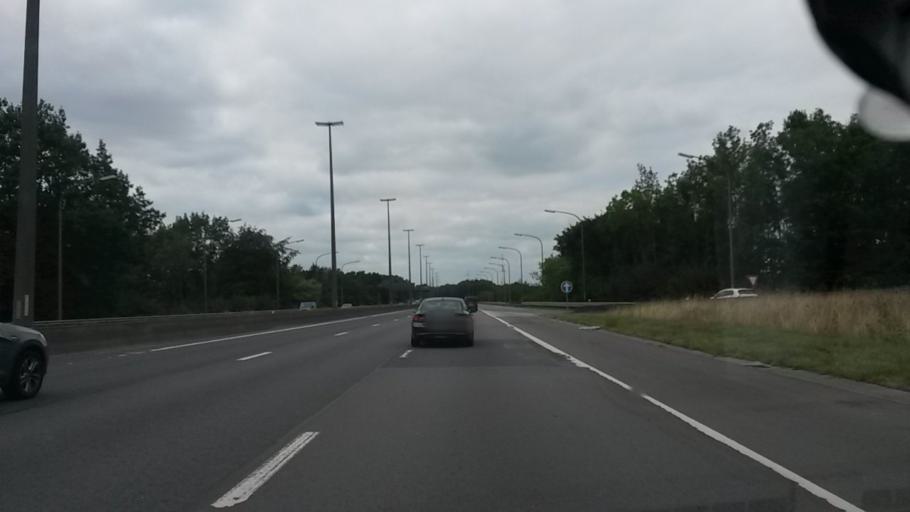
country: BE
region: Wallonia
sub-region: Province du Hainaut
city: Chapelle-lez-Herlaimont
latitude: 50.4889
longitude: 4.2663
